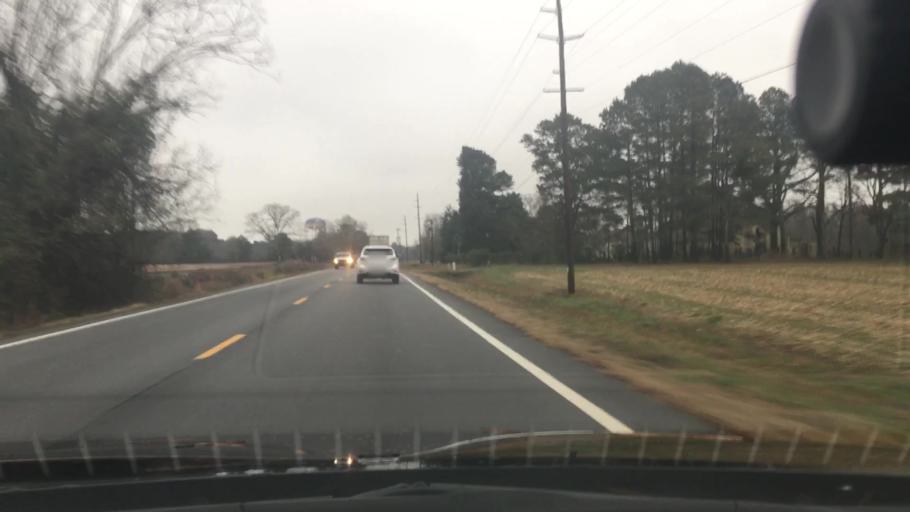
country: US
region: Georgia
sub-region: Coweta County
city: Senoia
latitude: 33.3100
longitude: -84.6044
